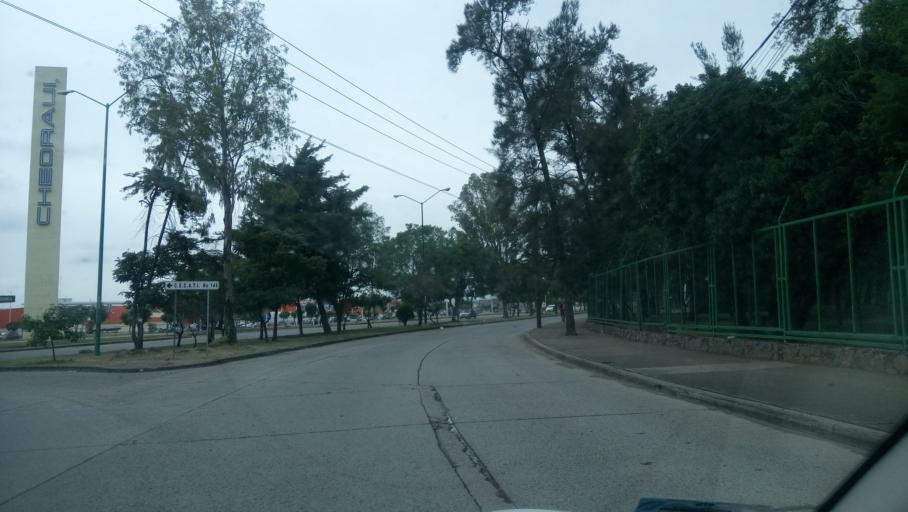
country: MX
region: Guanajuato
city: Leon
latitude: 21.1446
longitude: -101.6571
